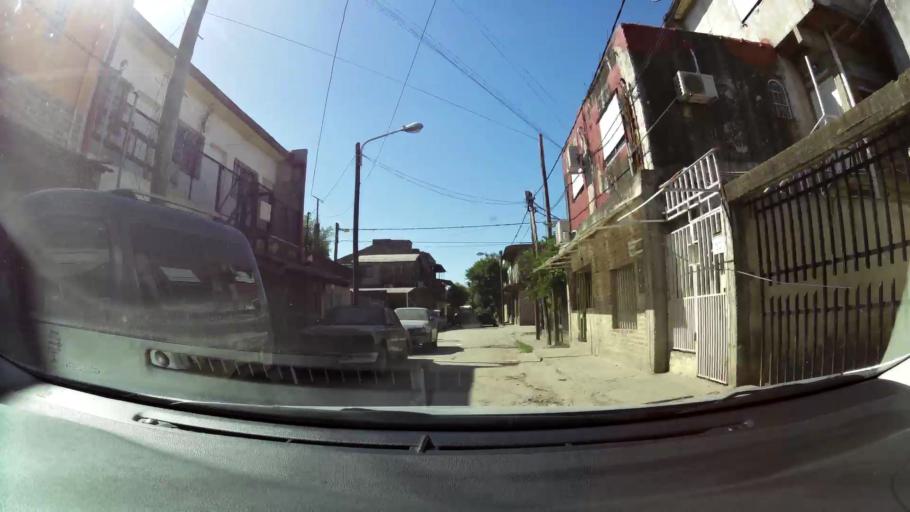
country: AR
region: Buenos Aires F.D.
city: Villa Lugano
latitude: -34.7061
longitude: -58.4740
